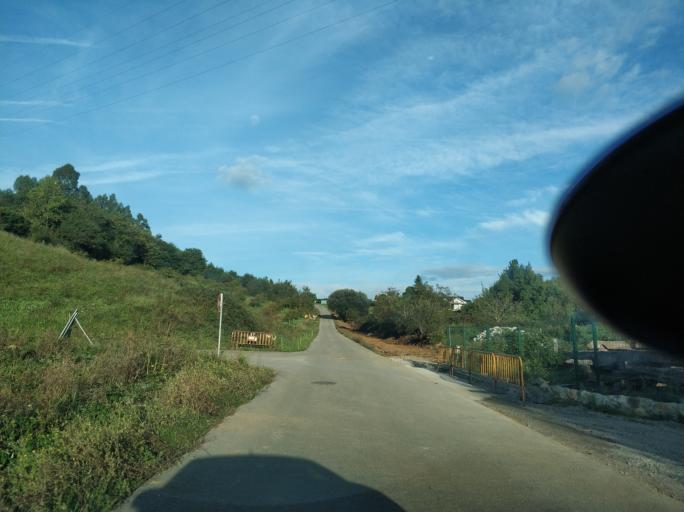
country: ES
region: Cantabria
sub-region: Provincia de Cantabria
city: Miengo
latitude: 43.4060
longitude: -3.9558
